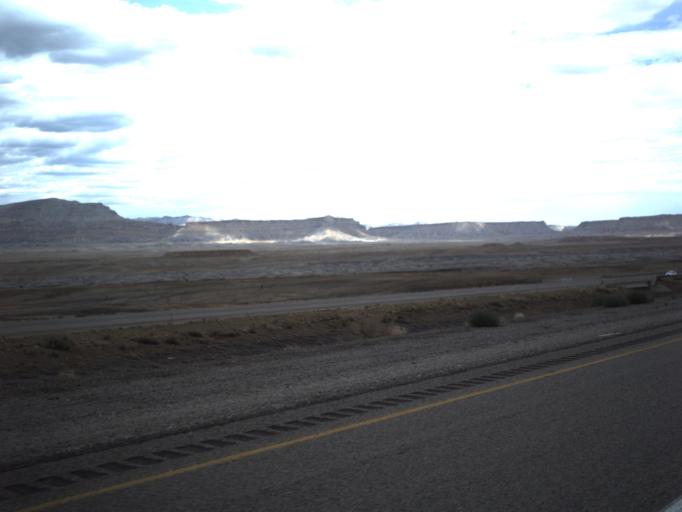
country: US
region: Utah
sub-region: Grand County
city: Moab
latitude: 38.9660
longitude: -110.0813
